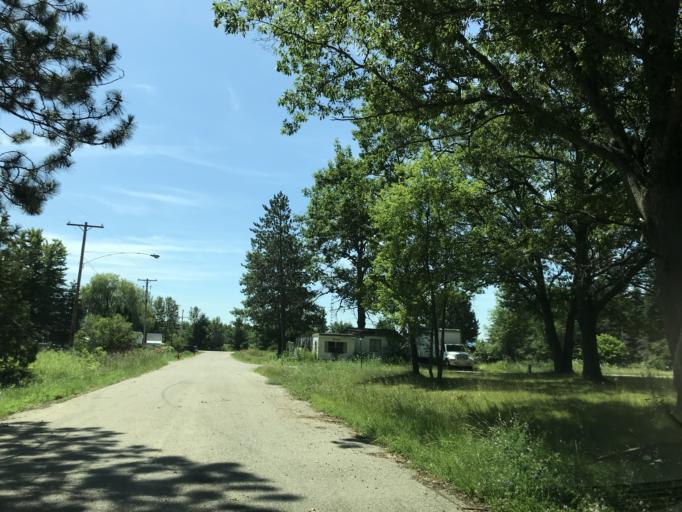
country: US
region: Michigan
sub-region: Roscommon County
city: Houghton Lake
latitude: 44.3296
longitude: -84.9431
